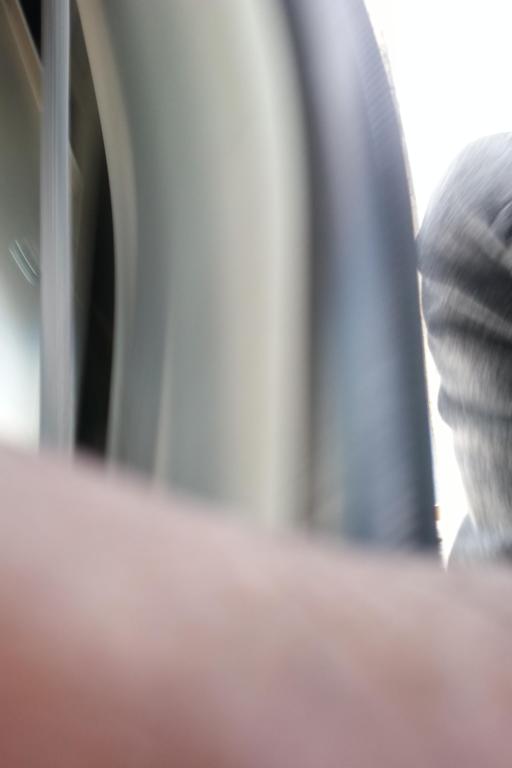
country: CA
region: Quebec
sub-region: Laurentides
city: Sainte-Marthe-sur-le-Lac
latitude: 45.5792
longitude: -73.9903
